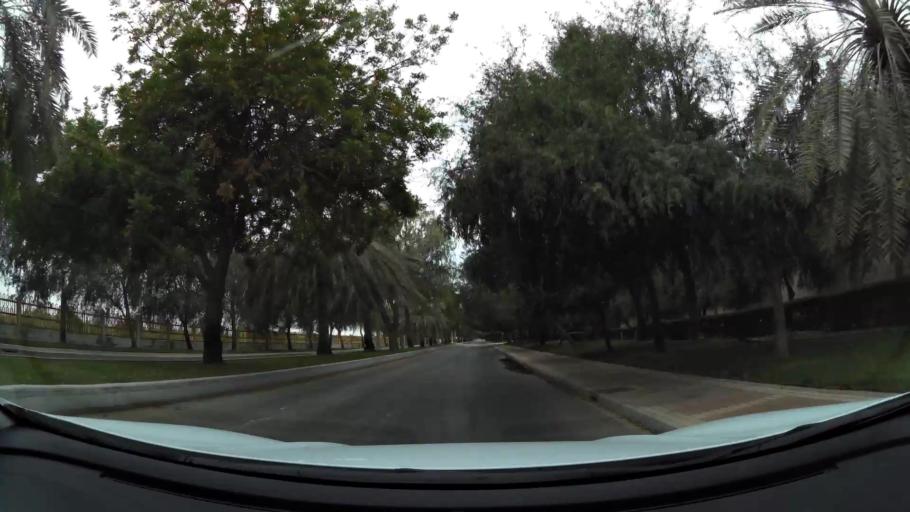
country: AE
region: Abu Dhabi
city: Abu Dhabi
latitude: 24.4260
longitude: 54.3843
